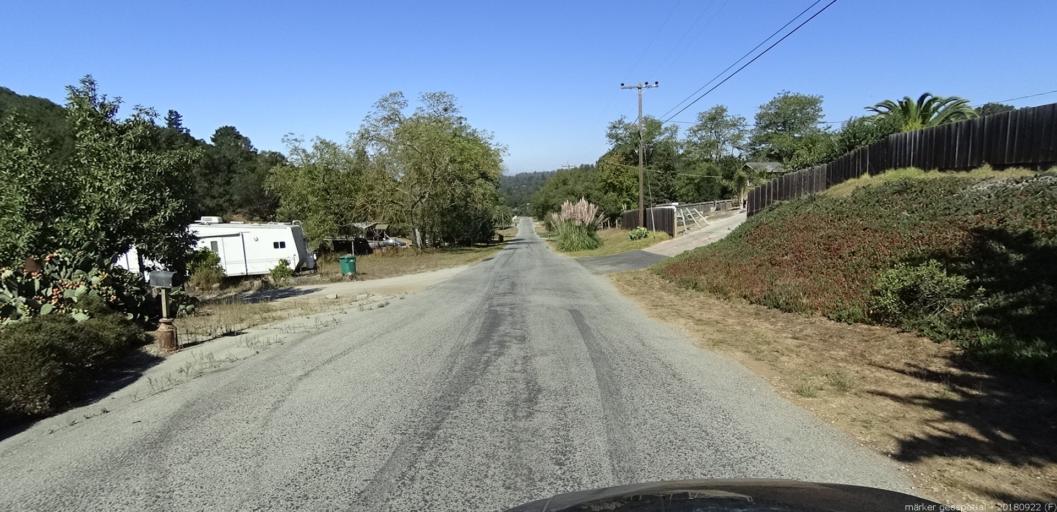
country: US
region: California
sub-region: Monterey County
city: Prunedale
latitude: 36.8082
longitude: -121.6278
